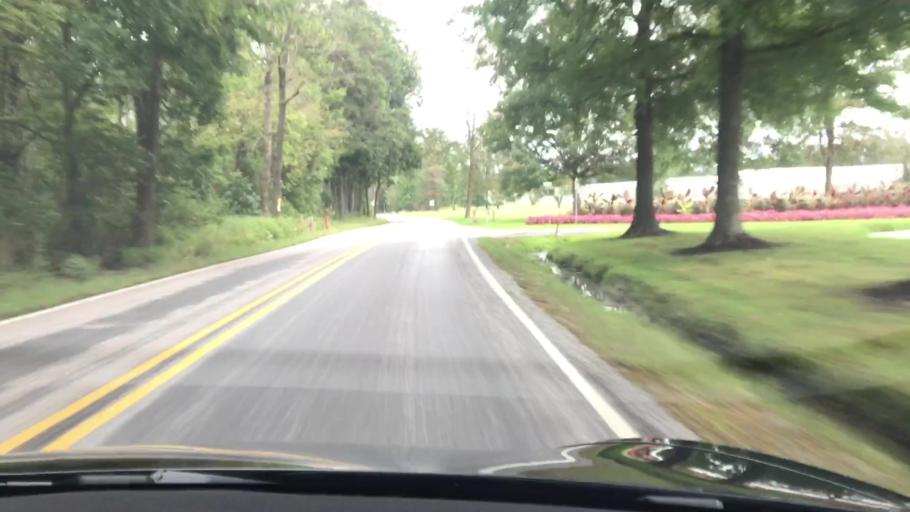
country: US
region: Pennsylvania
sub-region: York County
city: Dillsburg
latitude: 40.0616
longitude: -77.0781
